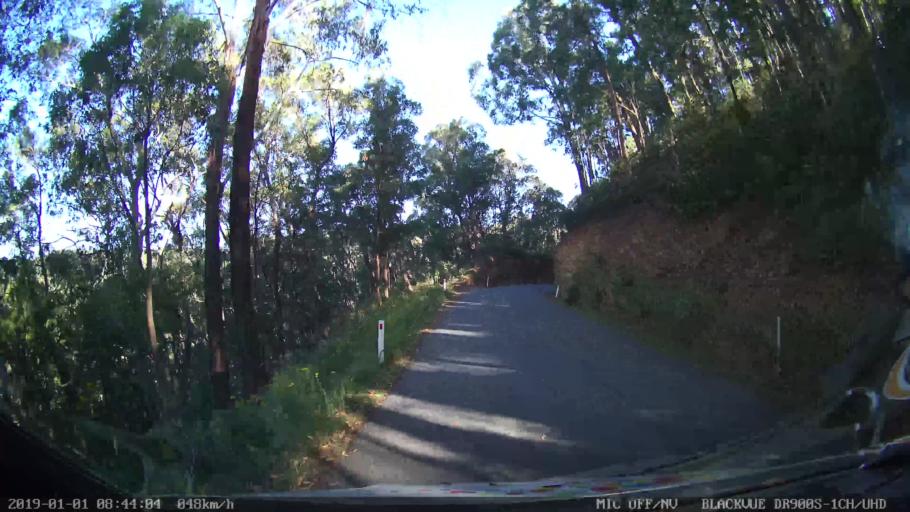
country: AU
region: New South Wales
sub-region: Snowy River
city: Jindabyne
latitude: -36.3131
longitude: 148.1903
